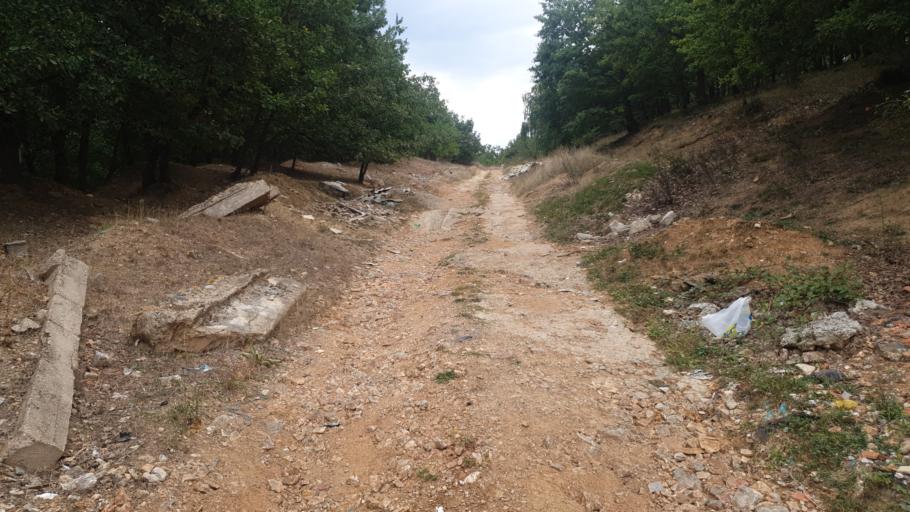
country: MK
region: Kicevo
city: Zajas
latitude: 41.5726
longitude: 20.9454
